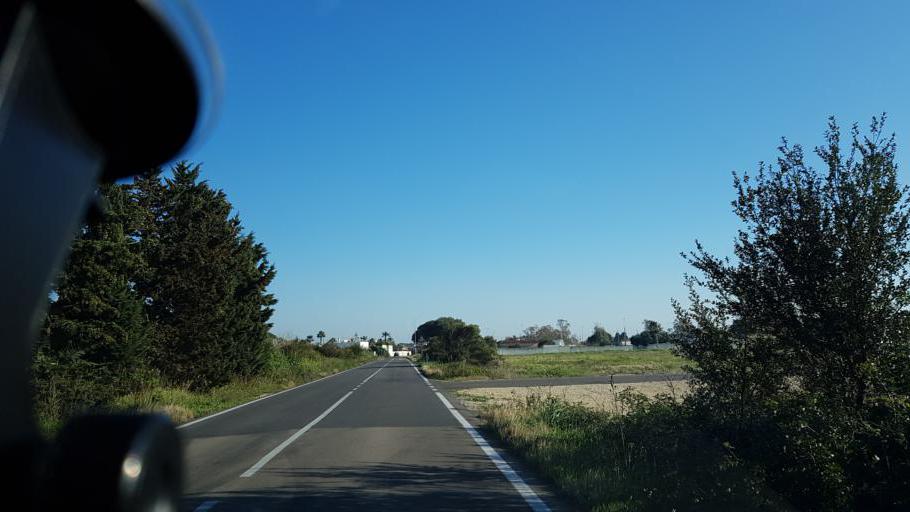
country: IT
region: Apulia
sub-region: Provincia di Lecce
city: Merine
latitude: 40.4334
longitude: 18.2408
